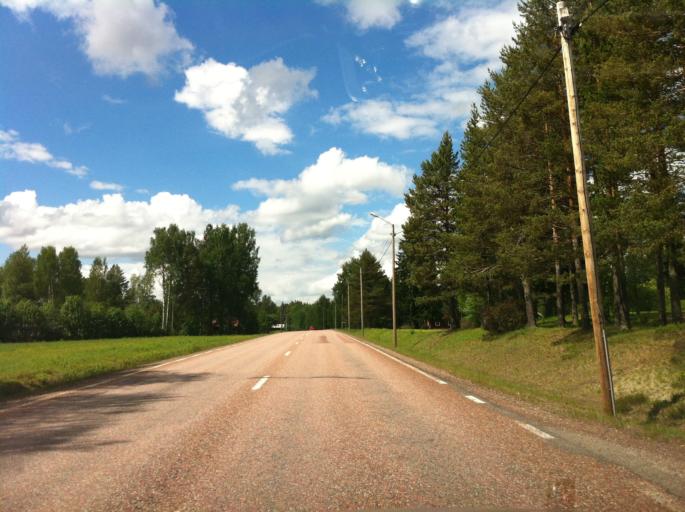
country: SE
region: Dalarna
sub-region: Malung-Saelens kommun
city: Malung
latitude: 60.7068
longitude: 13.6548
